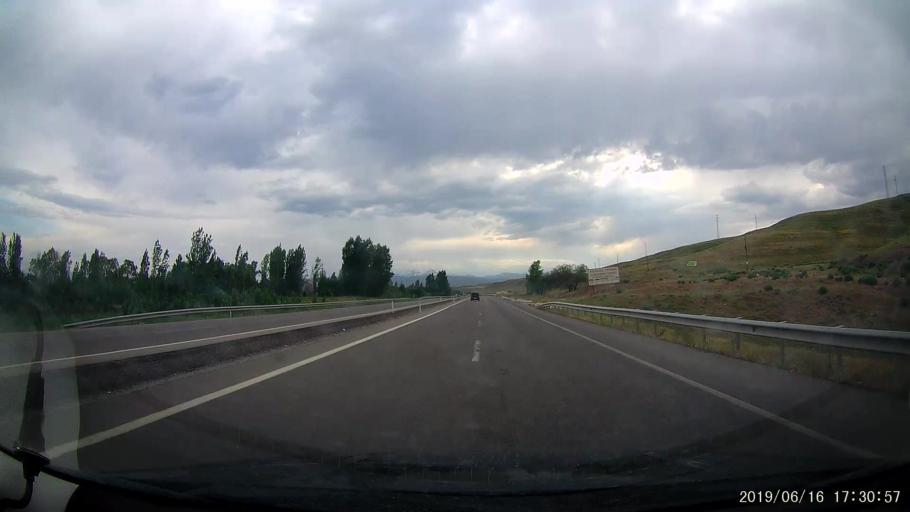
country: TR
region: Erzincan
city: Tercan
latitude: 39.7751
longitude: 40.3349
